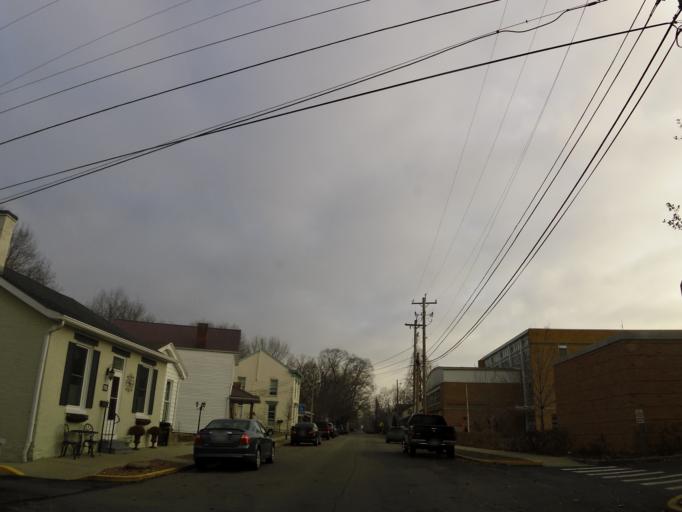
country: US
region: Indiana
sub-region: Jefferson County
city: Madison
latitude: 38.7391
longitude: -85.3888
